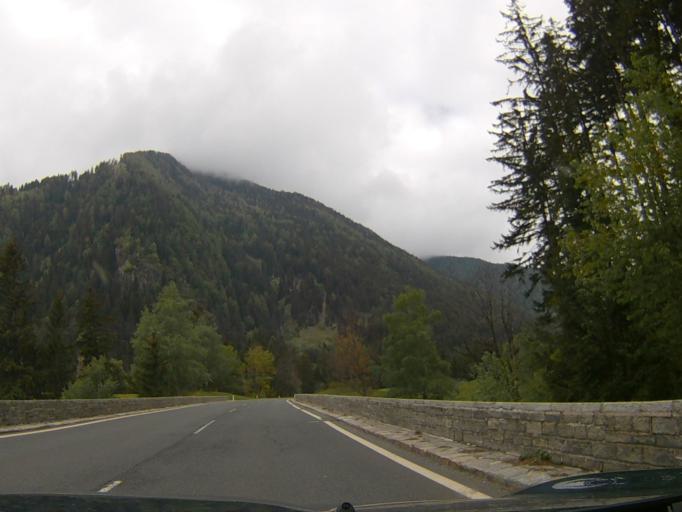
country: AT
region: Carinthia
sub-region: Politischer Bezirk Spittal an der Drau
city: Obervellach
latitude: 46.9462
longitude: 13.1837
